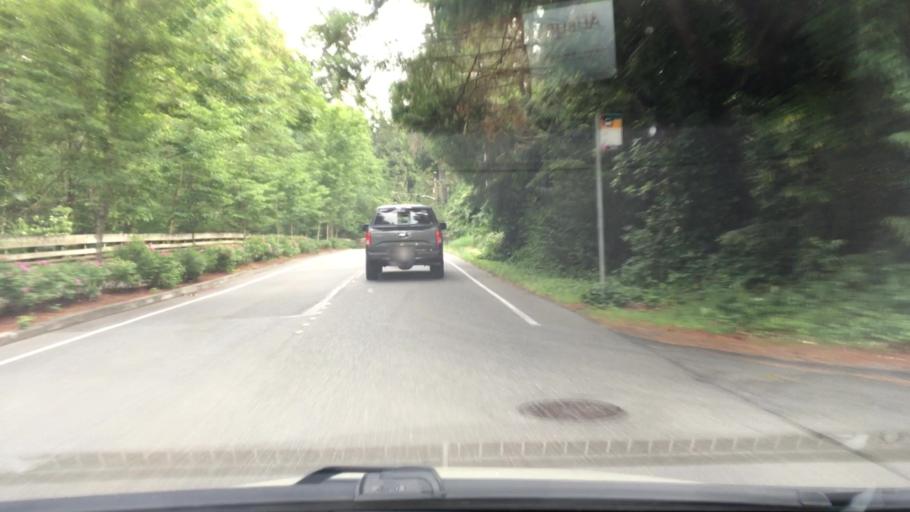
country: US
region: Washington
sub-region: King County
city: West Lake Sammamish
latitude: 47.5920
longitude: -122.1158
